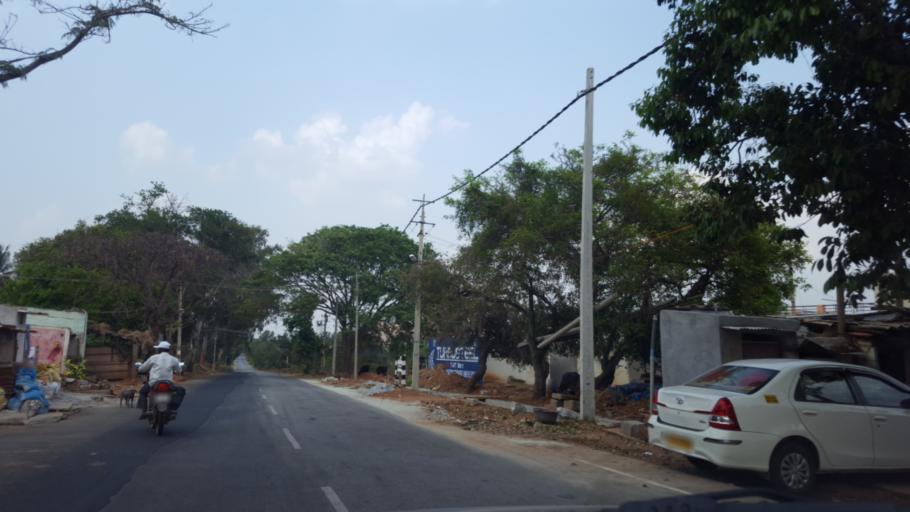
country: IN
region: Karnataka
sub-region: Chikkaballapur
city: Chik Ballapur
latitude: 13.3613
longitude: 77.6931
